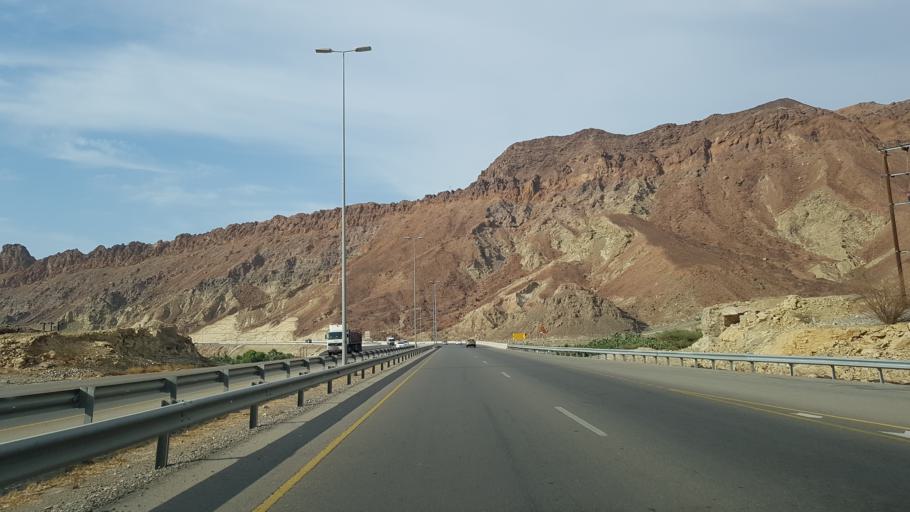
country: OM
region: Muhafazat ad Dakhiliyah
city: Bidbid
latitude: 23.4437
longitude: 58.1220
